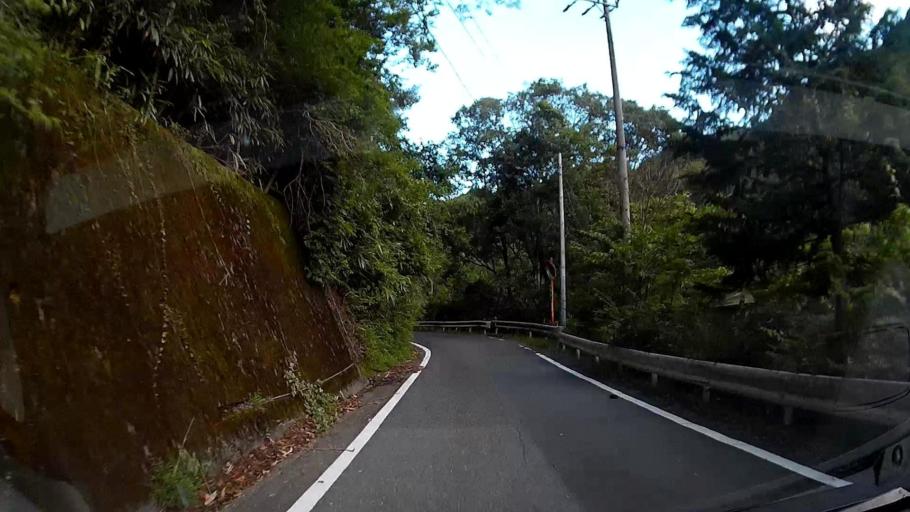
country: JP
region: Shizuoka
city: Shizuoka-shi
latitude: 35.1422
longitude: 138.2660
